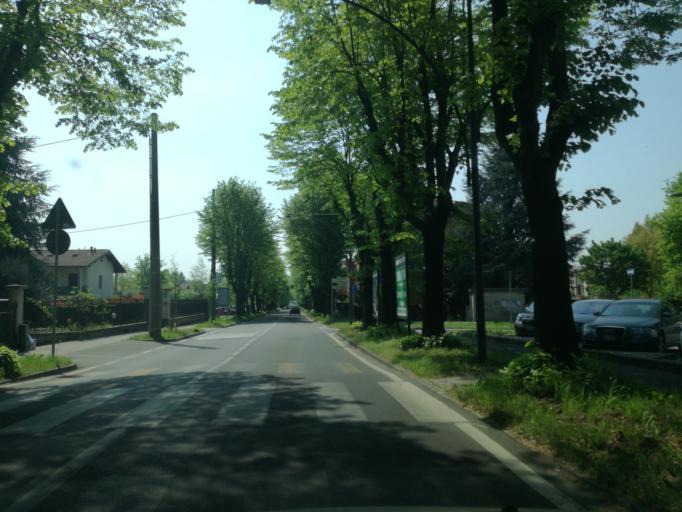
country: IT
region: Lombardy
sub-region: Provincia di Lecco
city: Paderno d'Adda
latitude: 45.6779
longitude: 9.4399
